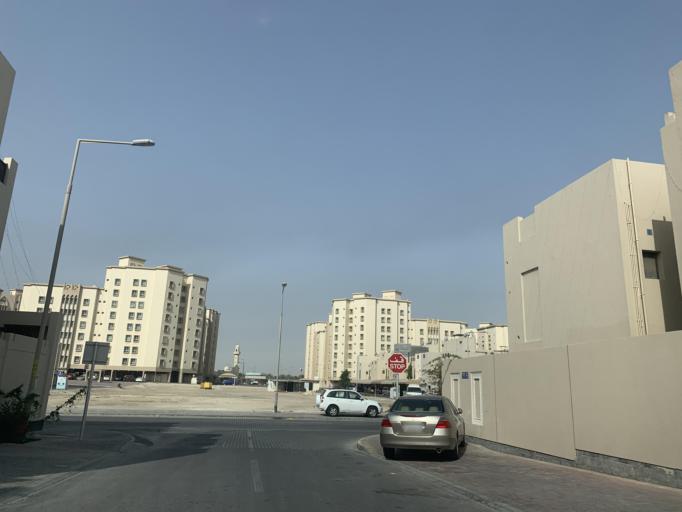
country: BH
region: Northern
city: Madinat `Isa
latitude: 26.1858
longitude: 50.5614
